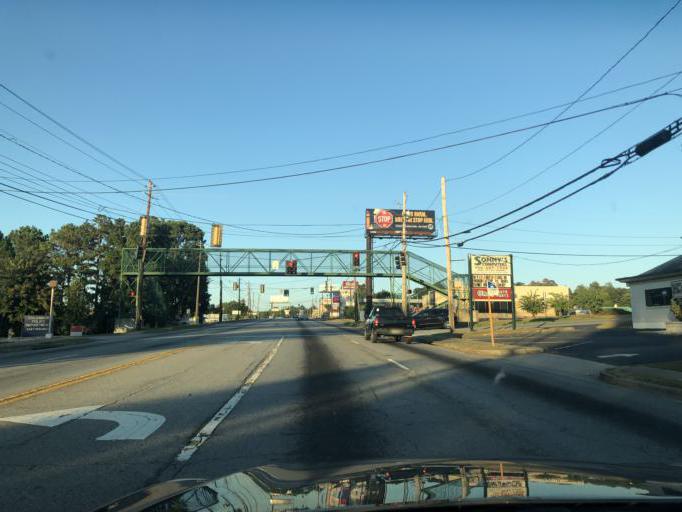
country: US
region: Georgia
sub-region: Muscogee County
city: Columbus
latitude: 32.4659
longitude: -84.9172
